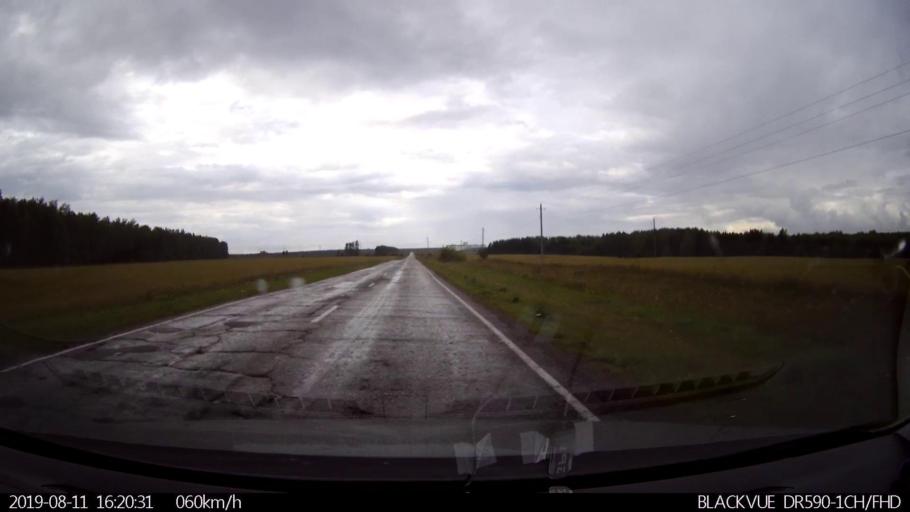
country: RU
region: Ulyanovsk
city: Mayna
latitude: 54.0724
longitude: 47.6025
